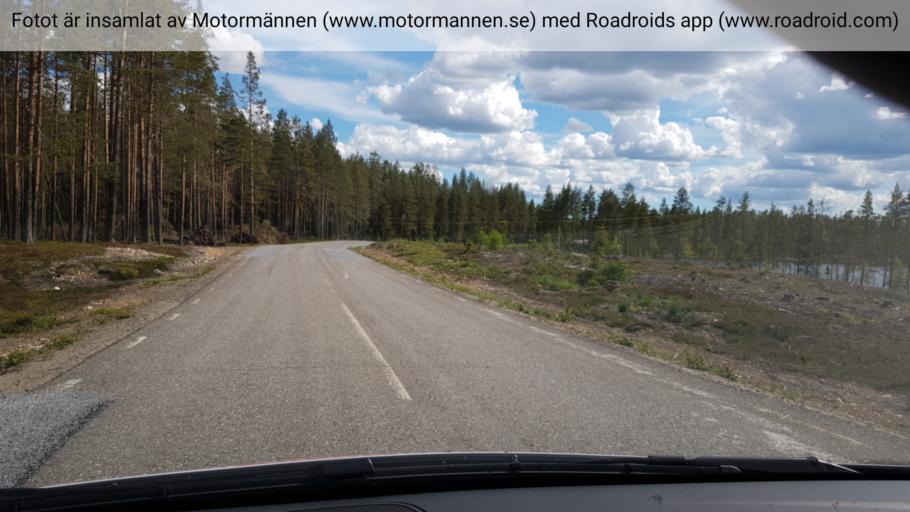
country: SE
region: Vaesterbotten
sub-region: Umea Kommun
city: Ersmark
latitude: 64.2083
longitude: 20.3247
